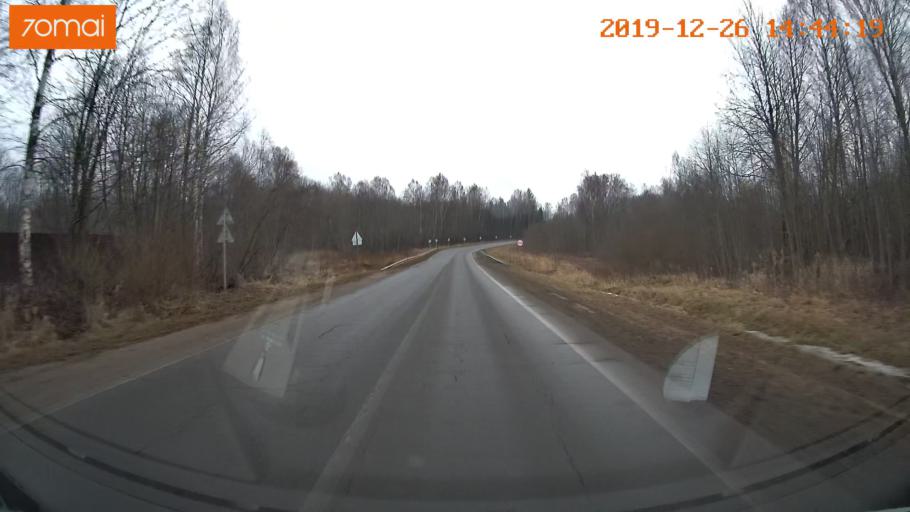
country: RU
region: Jaroslavl
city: Poshekhon'ye
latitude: 58.3493
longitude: 39.0492
